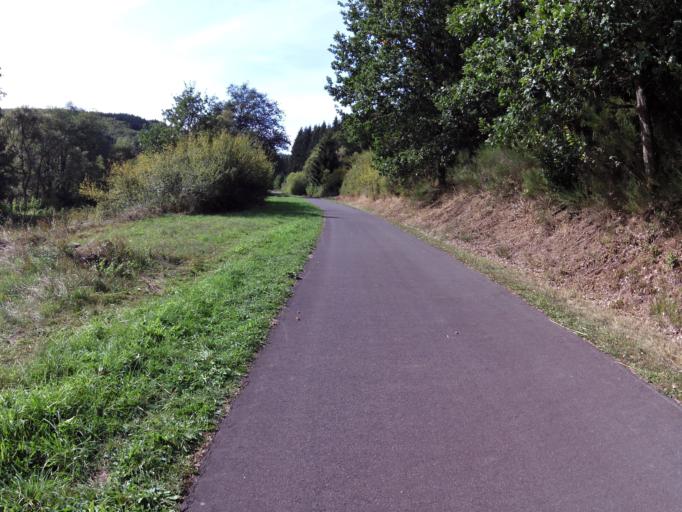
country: DE
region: Rheinland-Pfalz
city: Brandscheid
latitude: 50.1893
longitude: 6.2999
